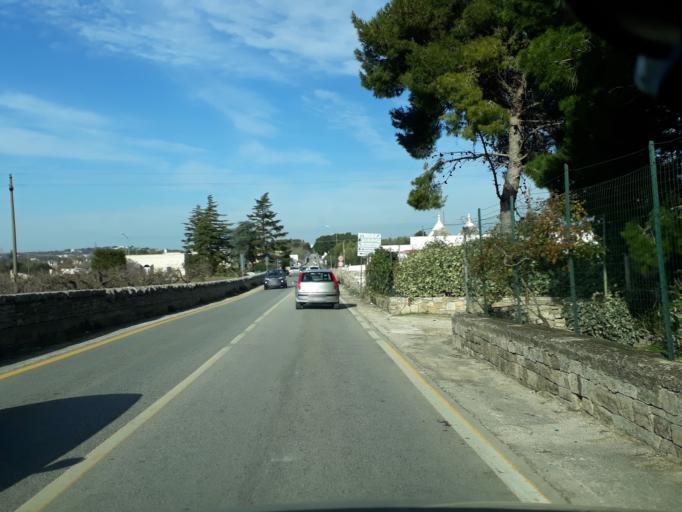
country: IT
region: Apulia
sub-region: Provincia di Taranto
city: Martina Franca
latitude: 40.7160
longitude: 17.3328
